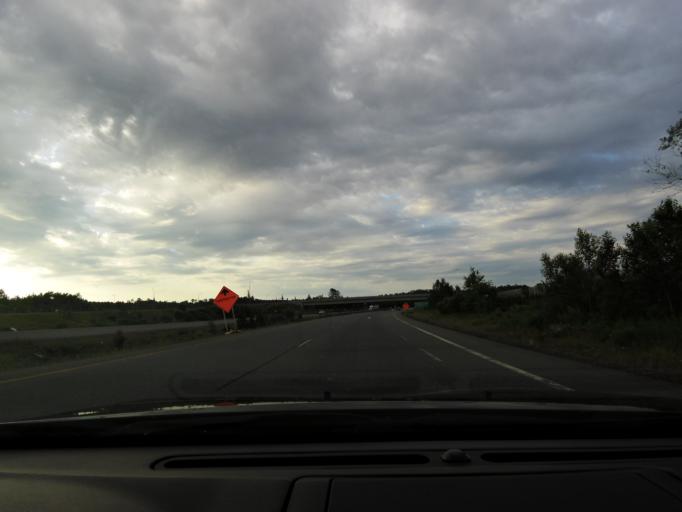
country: CA
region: Ontario
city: Huntsville
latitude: 45.3735
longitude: -79.2187
